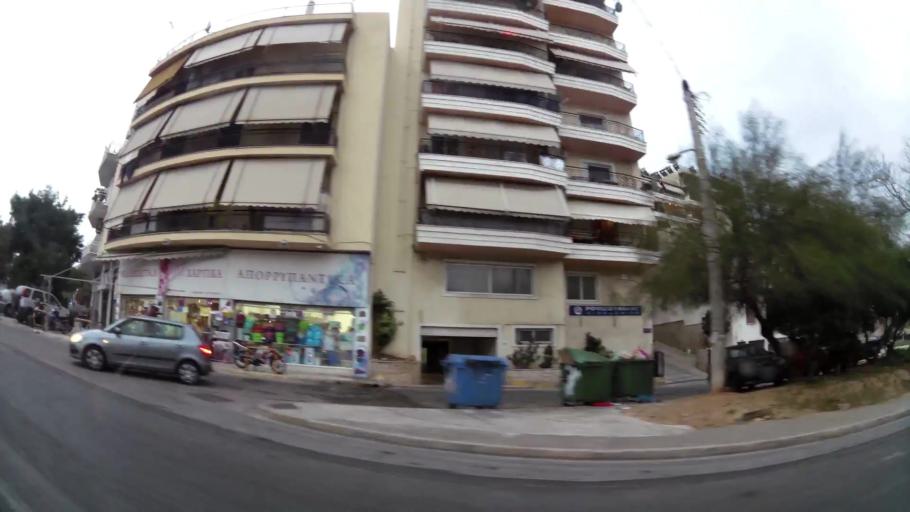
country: GR
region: Attica
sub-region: Nomos Piraios
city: Keratsini
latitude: 37.9632
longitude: 23.6125
